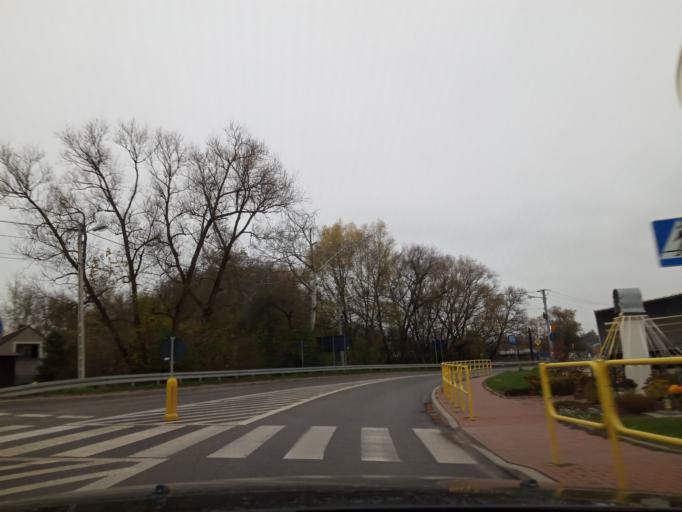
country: PL
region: Swietokrzyskie
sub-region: Powiat pinczowski
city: Dzialoszyce
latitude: 50.3588
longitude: 20.3508
